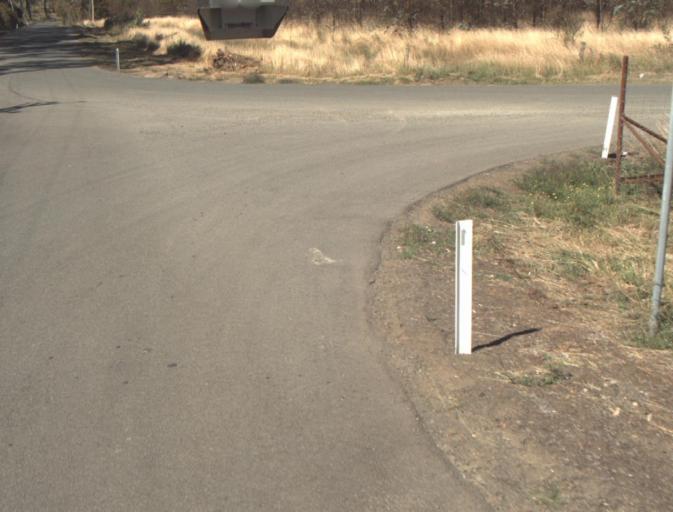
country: AU
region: Tasmania
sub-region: Launceston
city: Newstead
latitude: -41.3795
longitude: 147.2969
